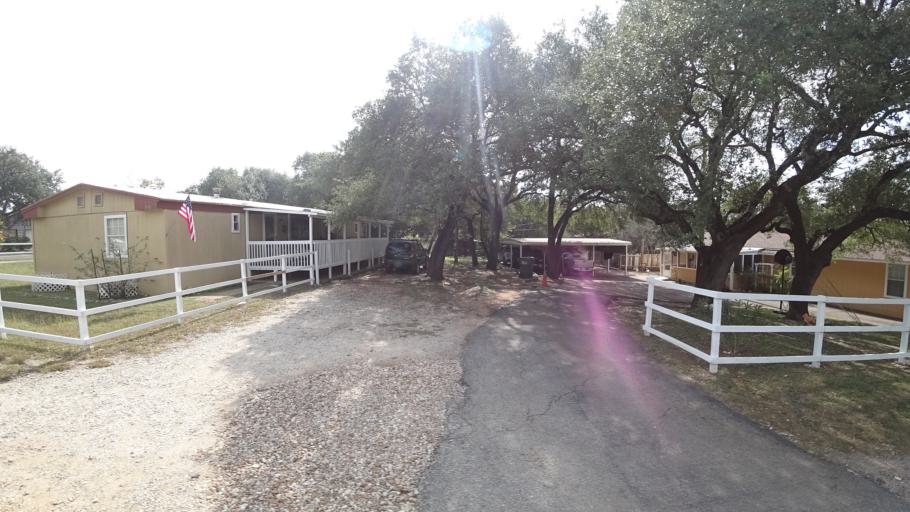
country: US
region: Texas
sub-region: Travis County
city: Hudson Bend
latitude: 30.3774
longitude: -97.9317
